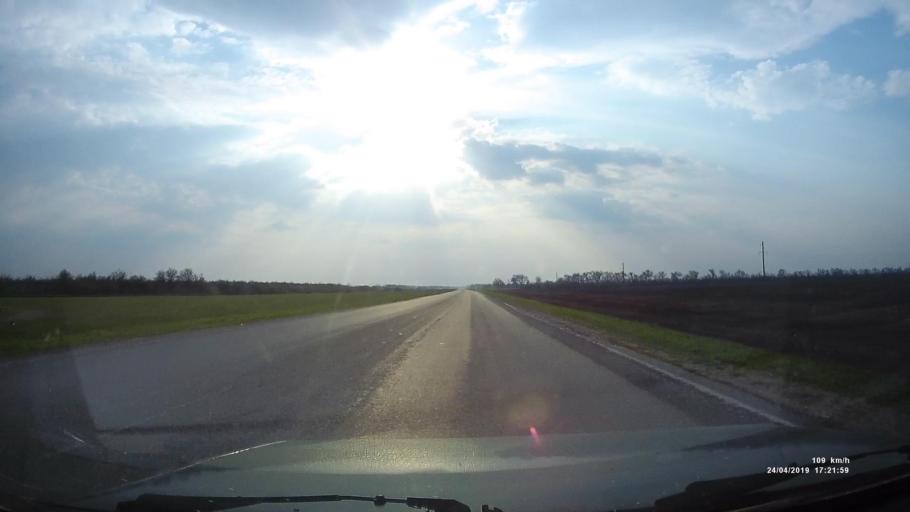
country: RU
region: Rostov
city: Gigant
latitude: 46.5201
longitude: 41.3180
